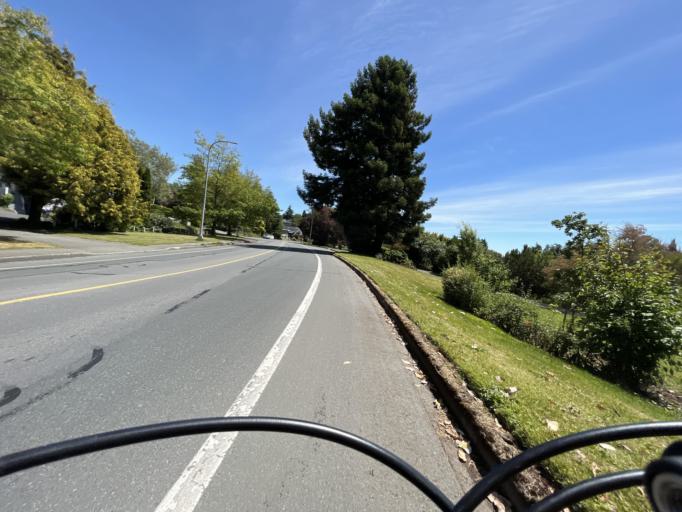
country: CA
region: British Columbia
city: Victoria
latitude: 48.4491
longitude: -123.4070
